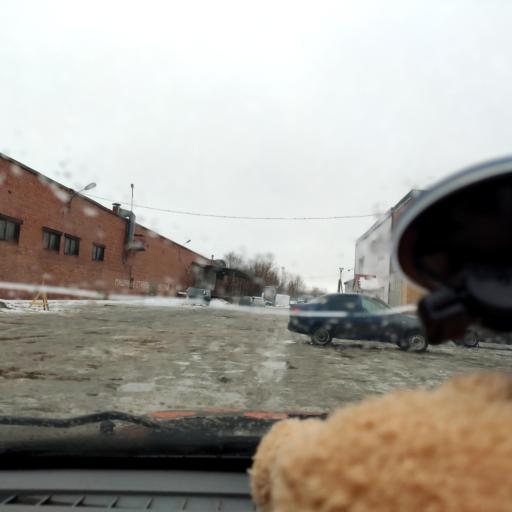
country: RU
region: Samara
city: Tol'yatti
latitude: 53.5617
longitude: 49.3086
